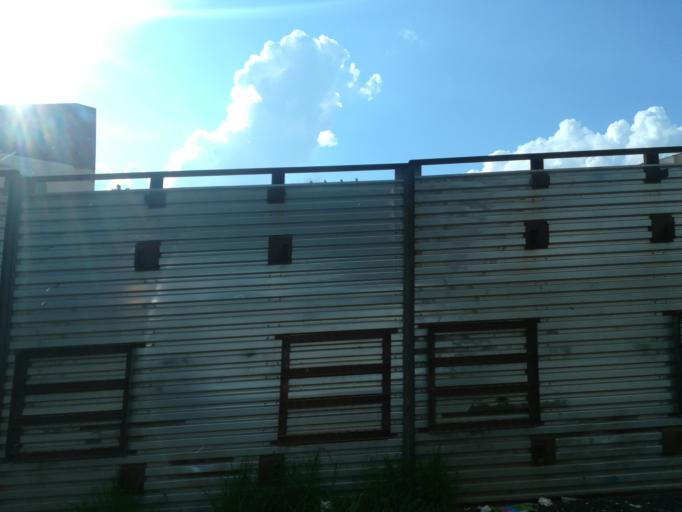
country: TR
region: Adana
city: Adana
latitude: 37.0431
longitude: 35.3025
